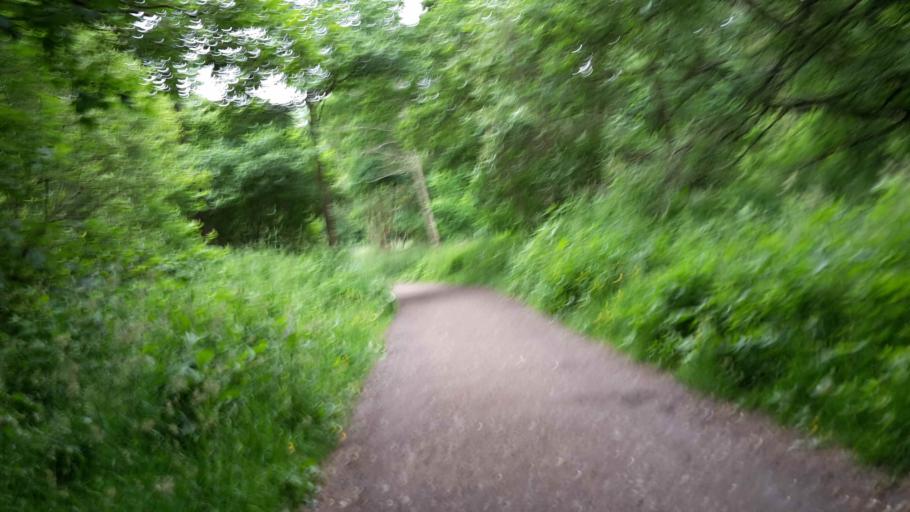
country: GB
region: Scotland
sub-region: South Lanarkshire
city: Uddingston
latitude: 55.8211
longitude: -4.0933
